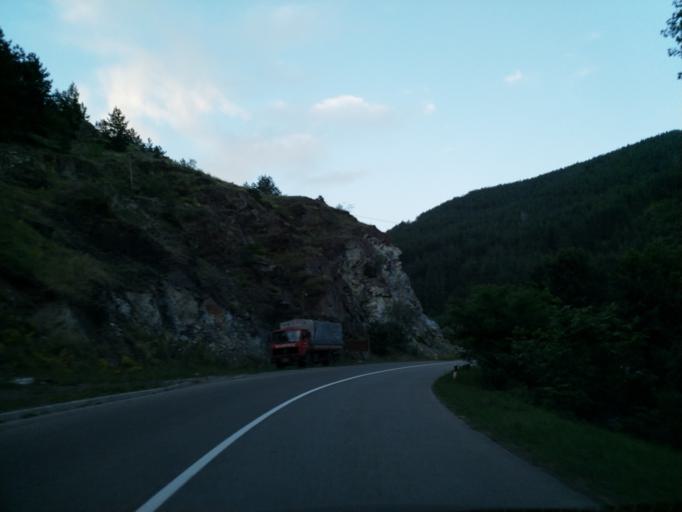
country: RS
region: Central Serbia
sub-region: Rasinski Okrug
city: Aleksandrovac
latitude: 43.3382
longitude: 20.9451
